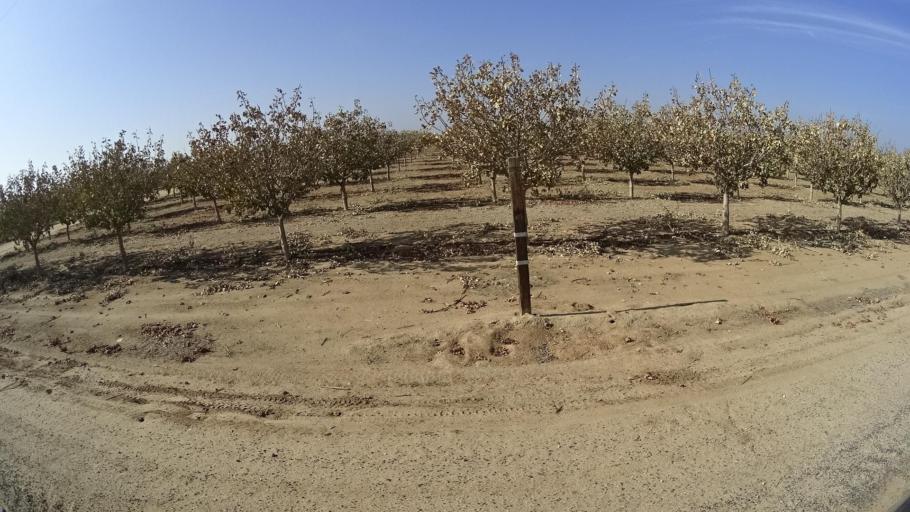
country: US
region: California
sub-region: Kern County
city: Shafter
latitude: 35.5409
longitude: -119.1513
